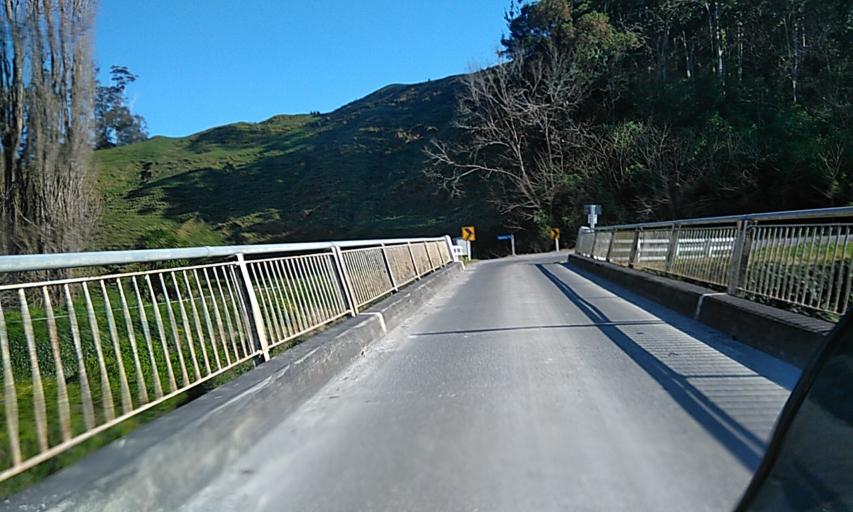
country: NZ
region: Gisborne
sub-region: Gisborne District
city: Gisborne
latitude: -38.5141
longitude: 178.0401
